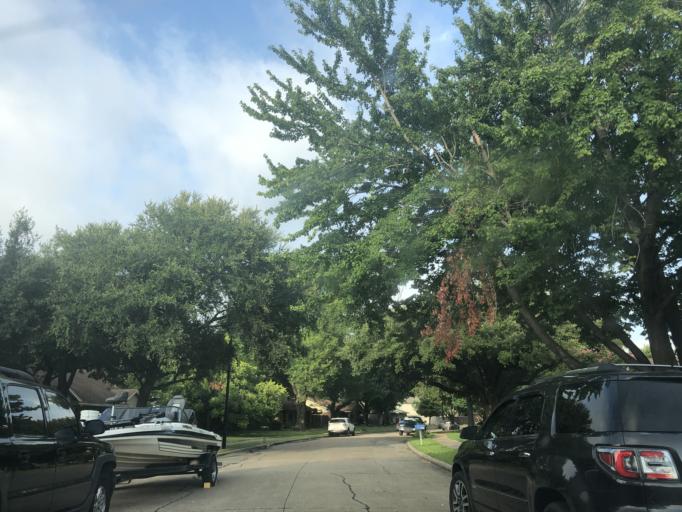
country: US
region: Texas
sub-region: Dallas County
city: Garland
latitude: 32.8531
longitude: -96.6283
